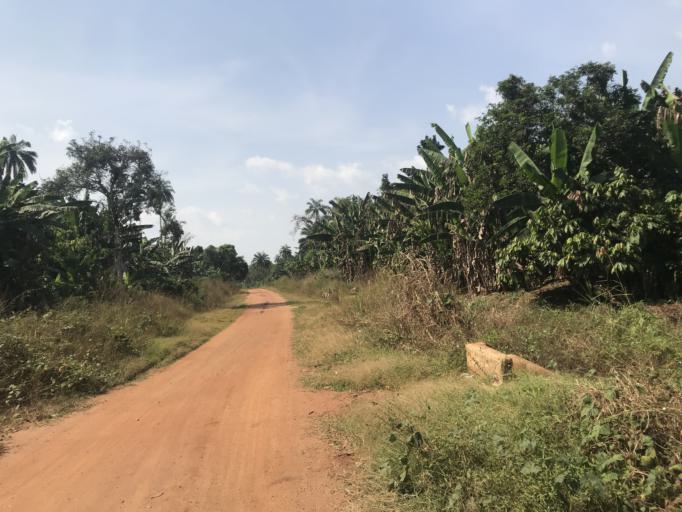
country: NG
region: Osun
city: Osu
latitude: 7.6337
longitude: 4.6665
